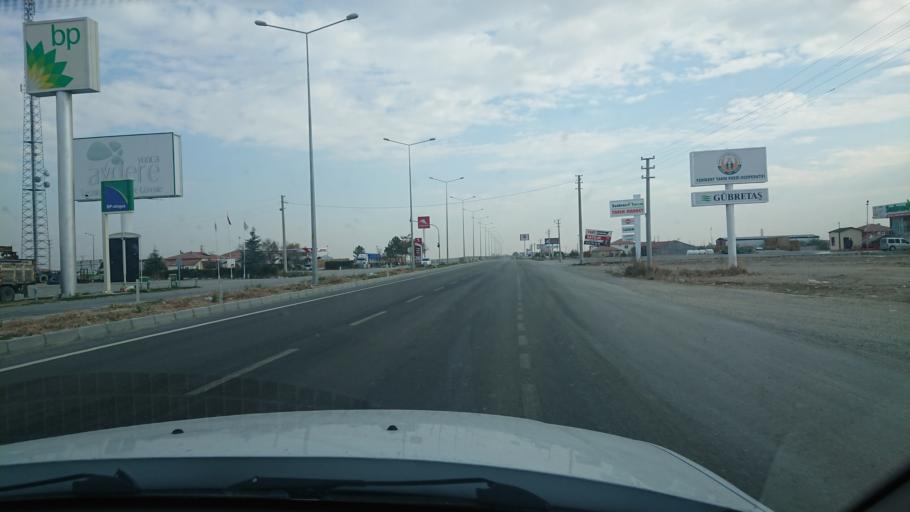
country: TR
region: Aksaray
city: Yesilova
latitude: 38.2918
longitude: 33.7630
